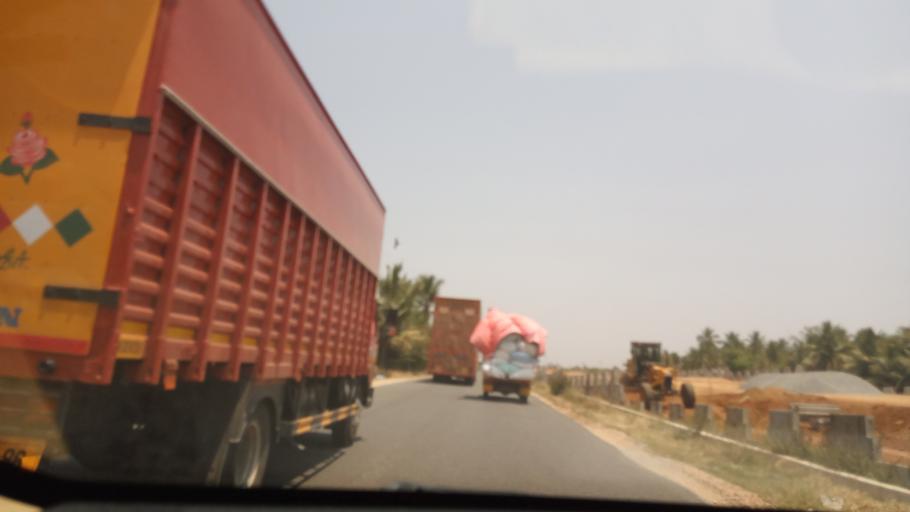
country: IN
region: Tamil Nadu
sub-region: Salem
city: Idappadi
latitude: 11.4931
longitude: 77.8615
